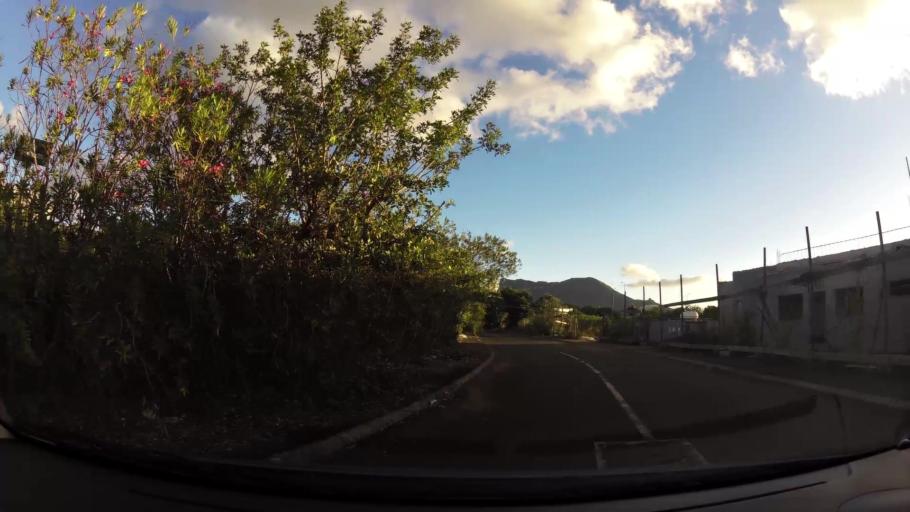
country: MU
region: Plaines Wilhems
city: Ebene
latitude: -20.2401
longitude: 57.4865
